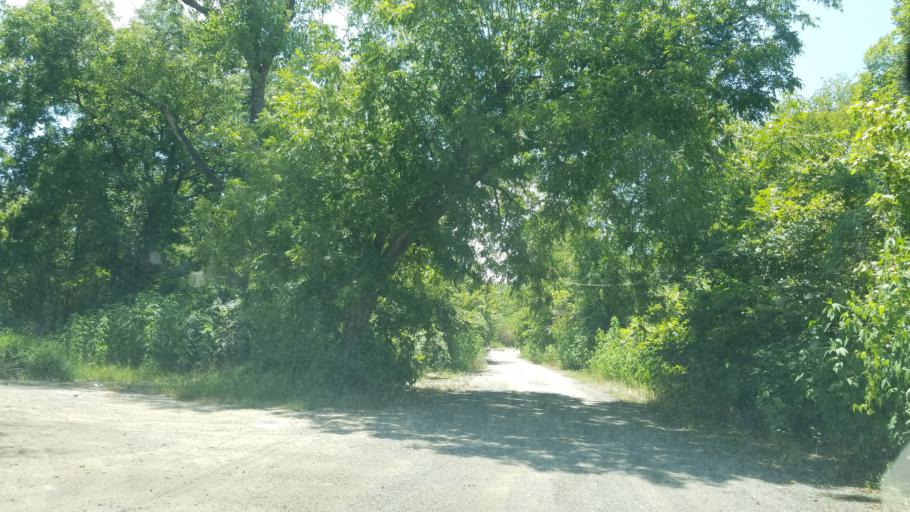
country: US
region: Texas
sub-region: Dallas County
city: Dallas
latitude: 32.7425
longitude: -96.7243
